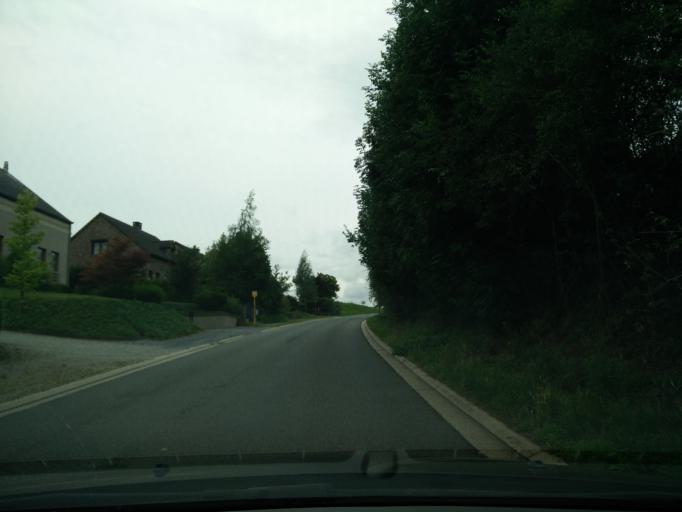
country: BE
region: Wallonia
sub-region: Province de Liege
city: Dalhem
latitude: 50.7166
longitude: 5.7136
